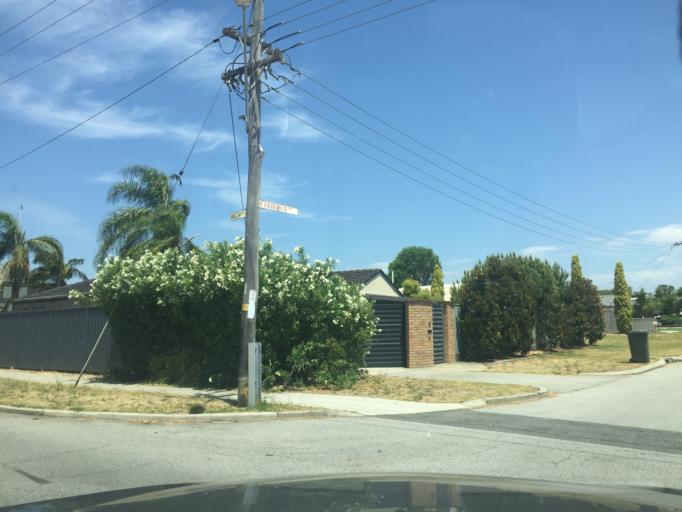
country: AU
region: Western Australia
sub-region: Canning
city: Ferndale
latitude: -32.0385
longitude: 115.9095
